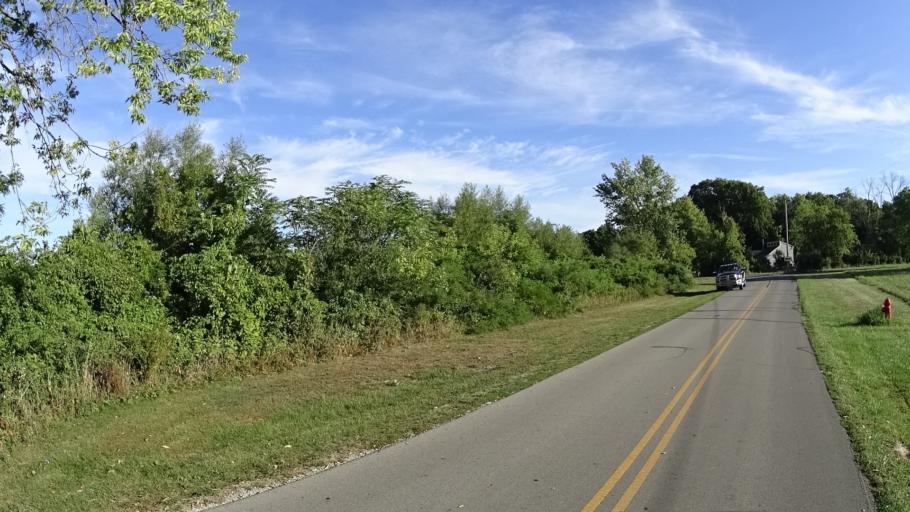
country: US
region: Ohio
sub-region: Erie County
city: Sandusky
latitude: 41.6109
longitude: -82.7230
